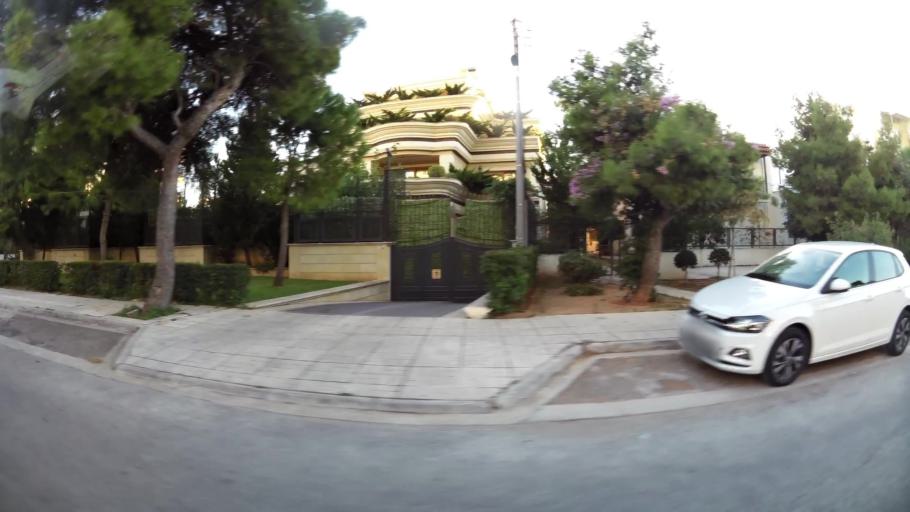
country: GR
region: Attica
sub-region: Nomarchia Athinas
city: Glyfada
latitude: 37.8707
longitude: 23.7498
